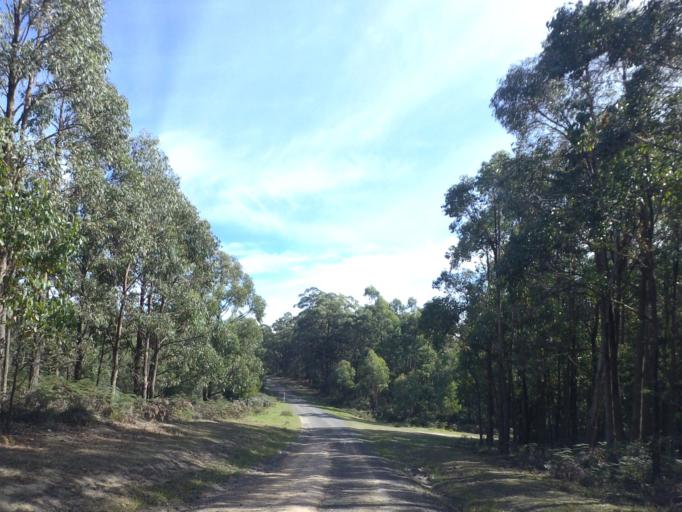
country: AU
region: Victoria
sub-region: Moorabool
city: Bacchus Marsh
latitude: -37.4555
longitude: 144.2094
